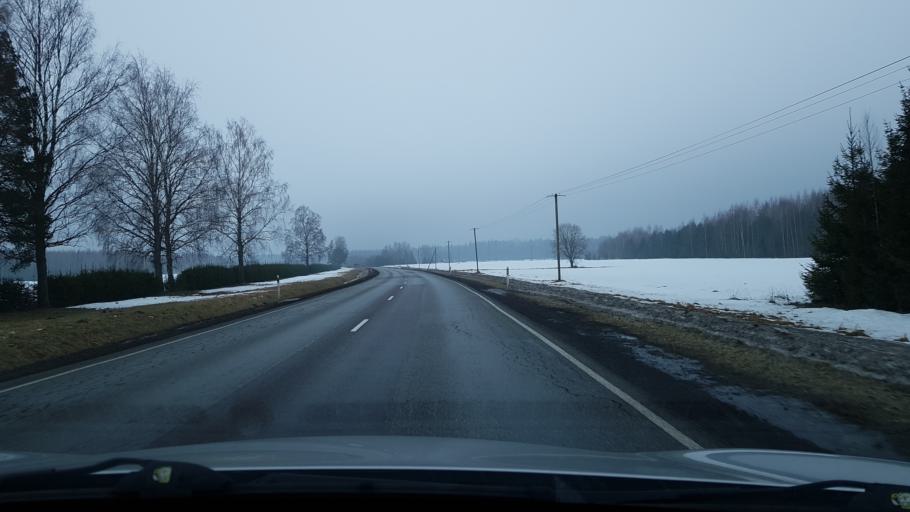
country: EE
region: Valgamaa
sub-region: Valga linn
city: Valga
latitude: 57.9033
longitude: 26.1733
